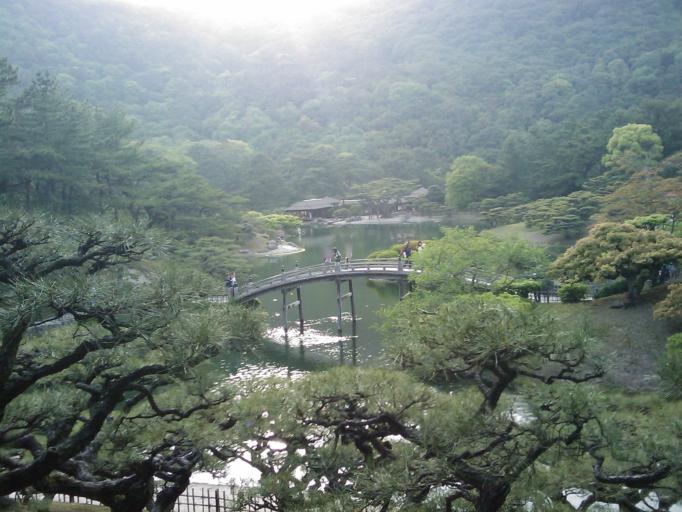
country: JP
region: Kagawa
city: Takamatsu-shi
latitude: 34.3324
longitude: 134.0432
